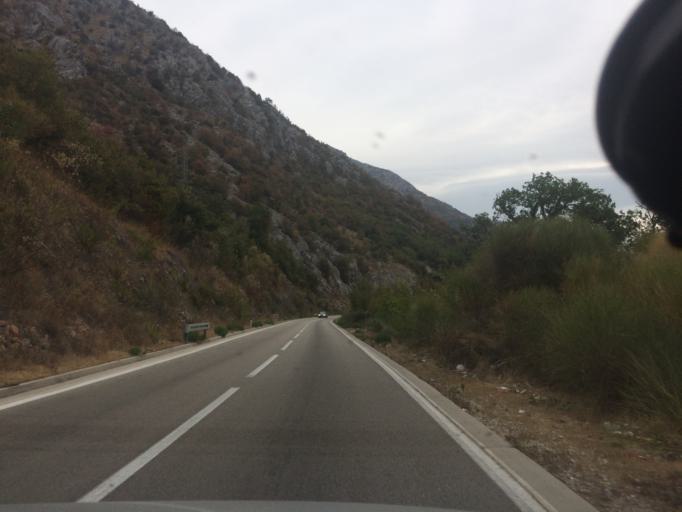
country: ME
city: Lipci
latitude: 42.4924
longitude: 18.6459
